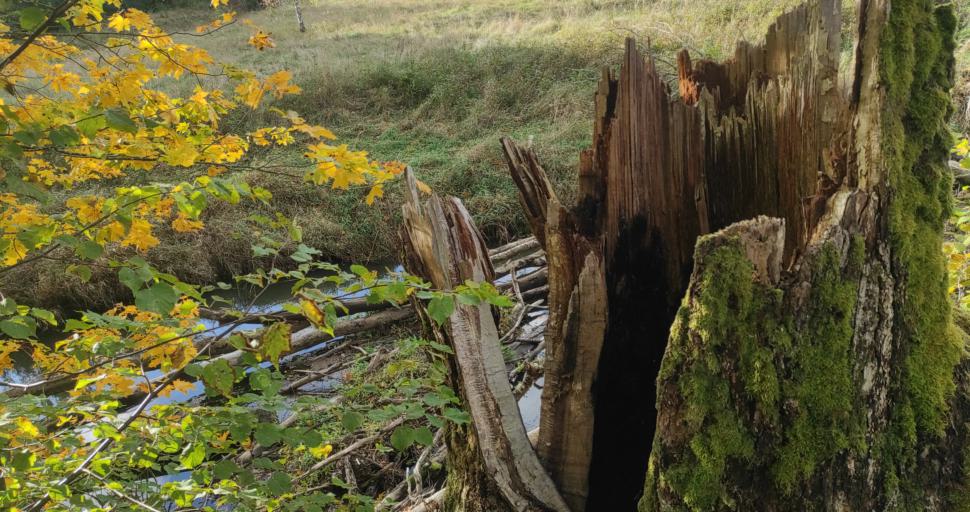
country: LV
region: Durbe
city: Liegi
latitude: 56.7342
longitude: 21.3734
